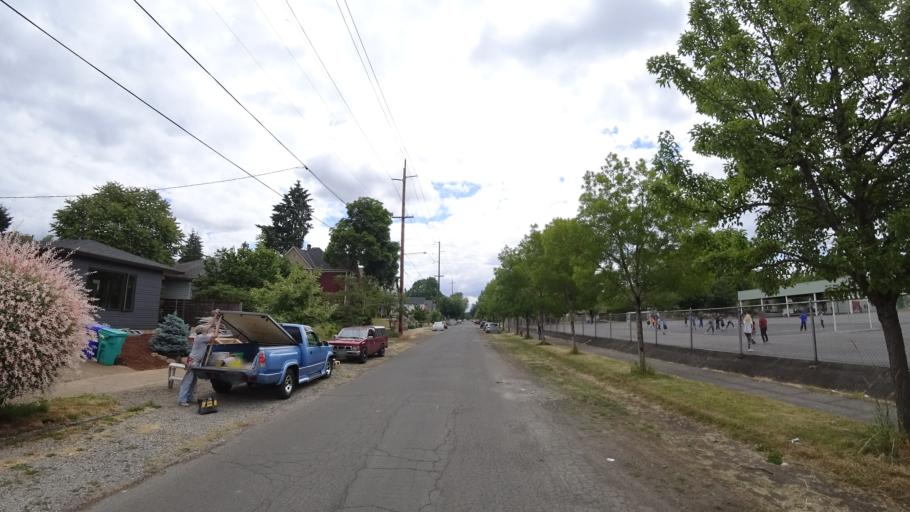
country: US
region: Oregon
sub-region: Washington County
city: West Haven
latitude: 45.5799
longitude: -122.7294
